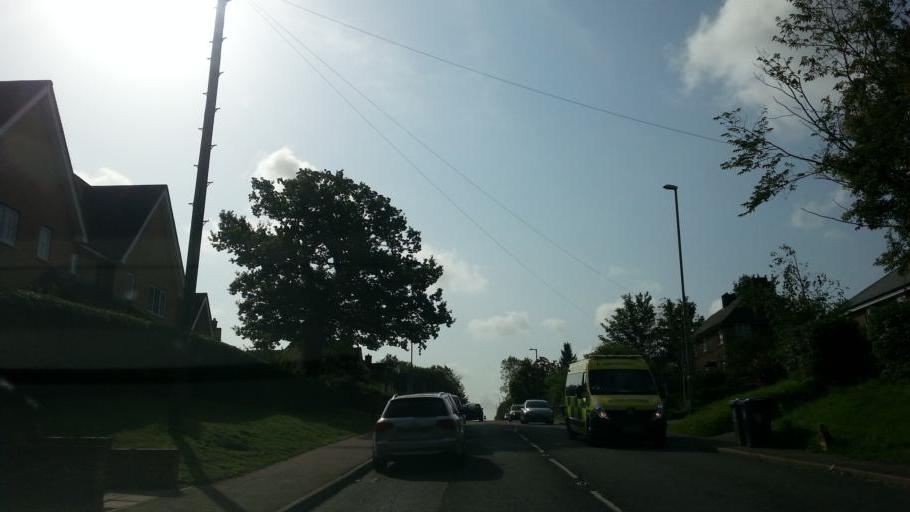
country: GB
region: England
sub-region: Cambridgeshire
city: Papworth Everard
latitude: 52.2452
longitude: -0.1149
